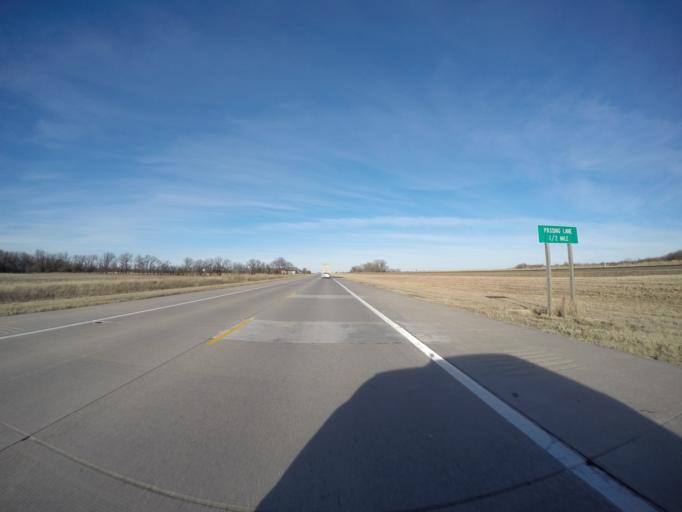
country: US
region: Kansas
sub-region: Harvey County
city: North Newton
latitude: 38.0808
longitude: -97.2943
